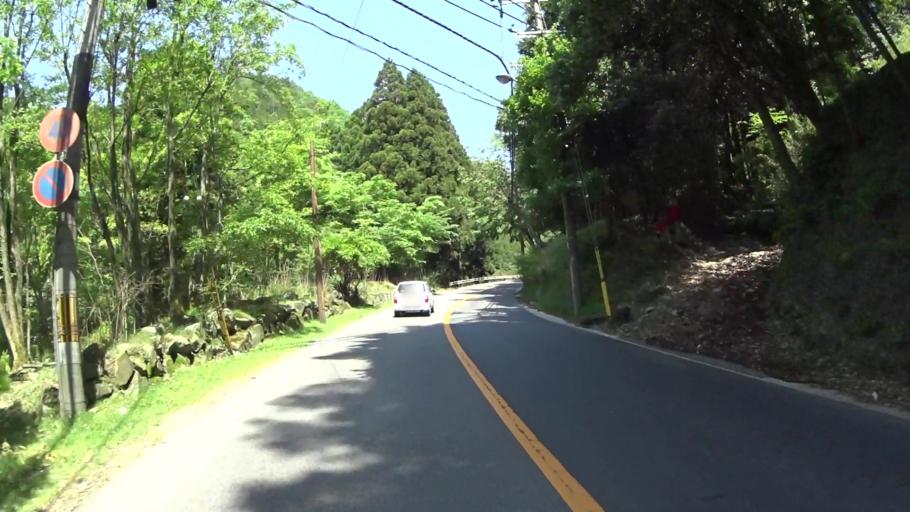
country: JP
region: Kyoto
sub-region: Kyoto-shi
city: Kamigyo-ku
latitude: 35.0919
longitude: 135.8223
